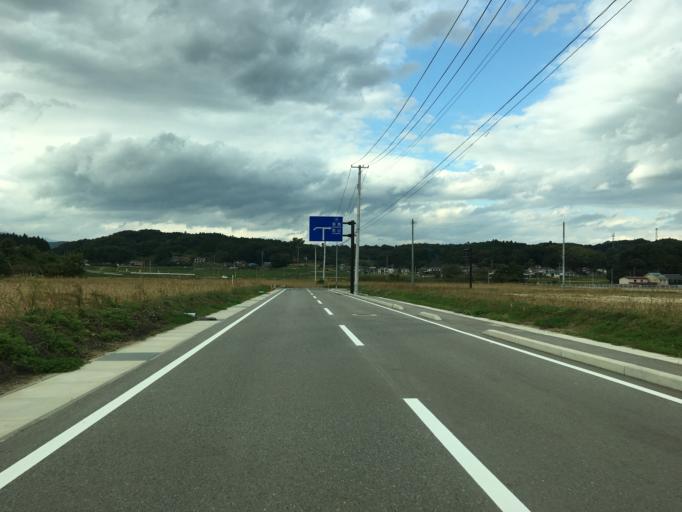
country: JP
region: Fukushima
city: Nihommatsu
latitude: 37.5595
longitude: 140.4035
